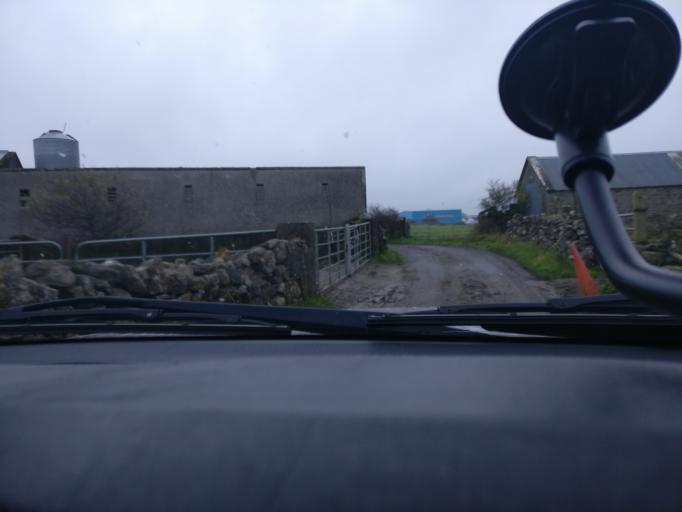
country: IE
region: Connaught
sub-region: County Galway
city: Loughrea
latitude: 53.2081
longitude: -8.5470
